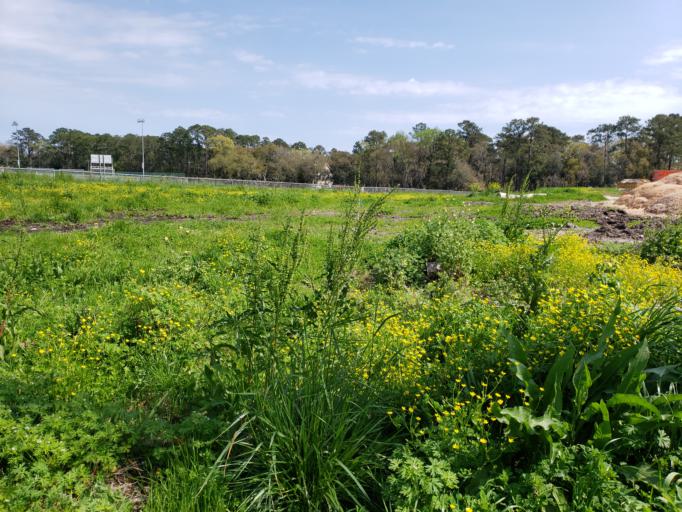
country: US
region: Georgia
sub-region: Chatham County
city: Wilmington Island
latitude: 32.0192
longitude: -80.9715
